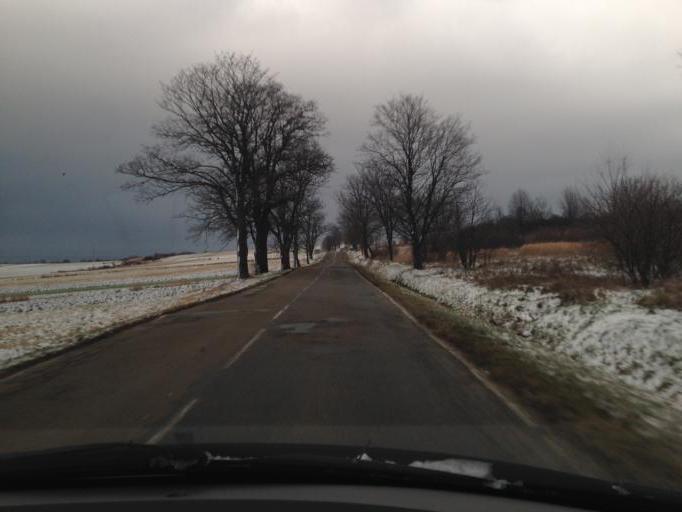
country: PL
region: Subcarpathian Voivodeship
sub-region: Powiat jasielski
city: Osiek Jasielski
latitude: 49.6103
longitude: 21.4958
